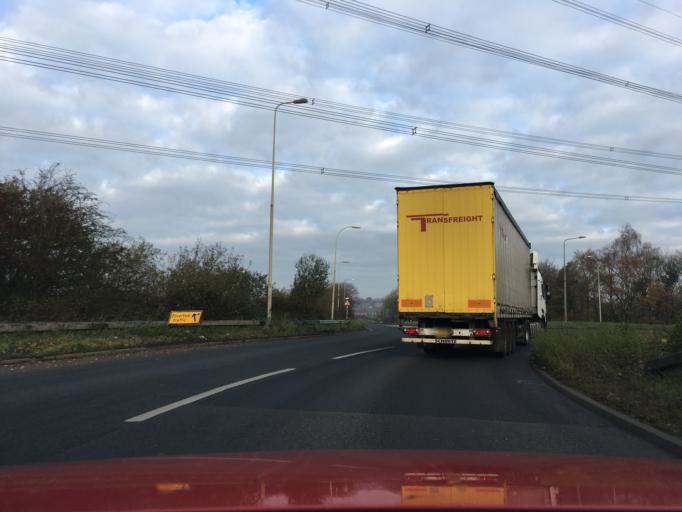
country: GB
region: England
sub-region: Staffordshire
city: Lichfield
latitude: 52.6631
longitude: -1.8168
